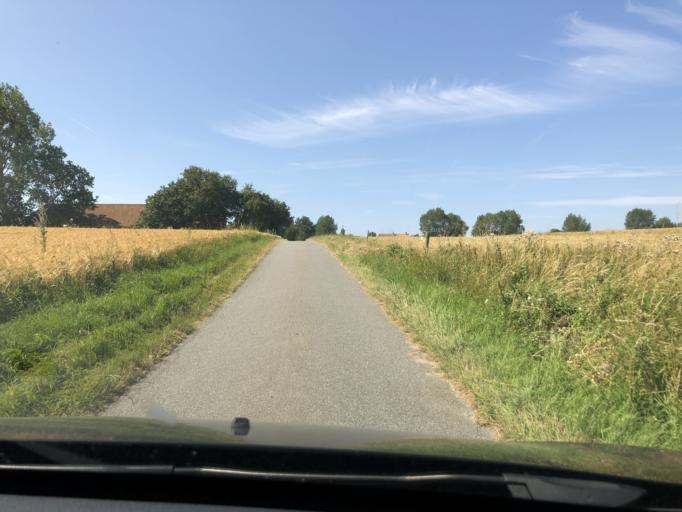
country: DK
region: South Denmark
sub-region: AEro Kommune
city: AEroskobing
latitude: 54.9116
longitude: 10.3246
